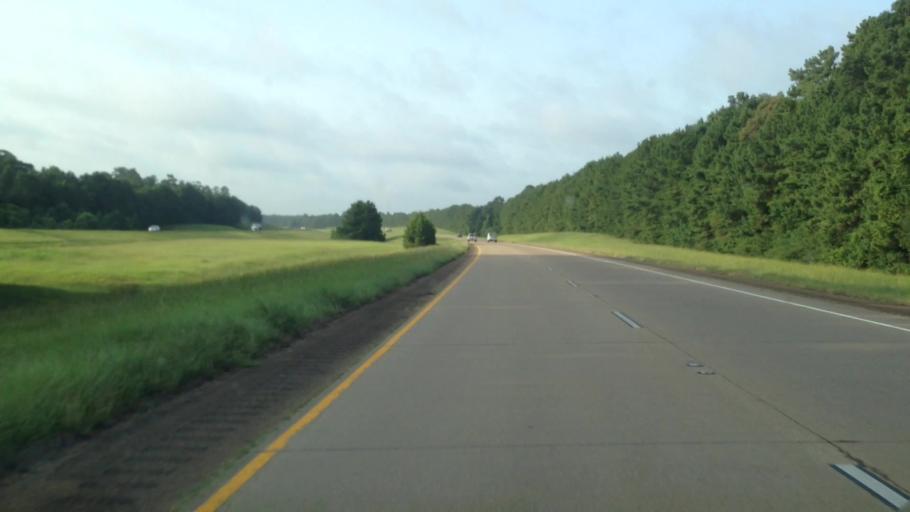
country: US
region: Louisiana
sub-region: Rapides Parish
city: Lecompte
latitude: 31.0969
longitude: -92.4456
